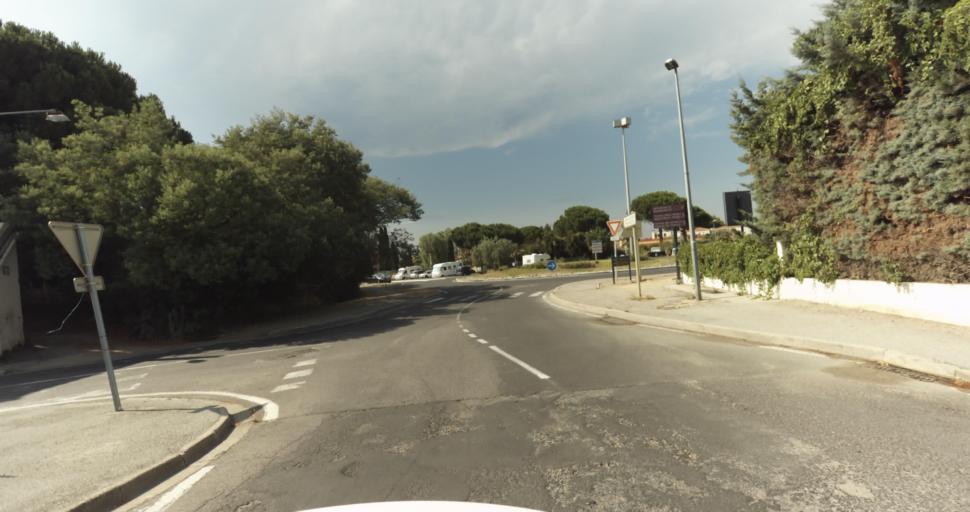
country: FR
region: Languedoc-Roussillon
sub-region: Departement des Pyrenees-Orientales
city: Elne
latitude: 42.6030
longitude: 2.9733
